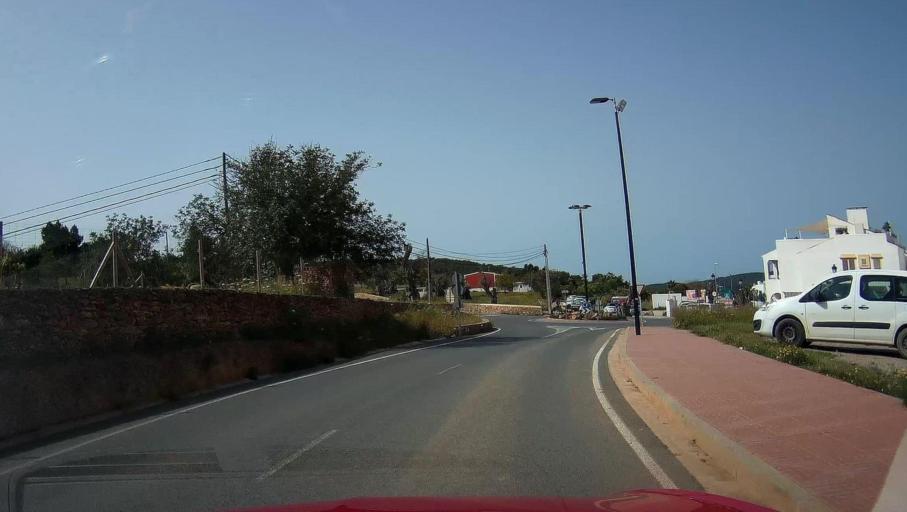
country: ES
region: Balearic Islands
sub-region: Illes Balears
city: Santa Eularia des Riu
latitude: 39.0336
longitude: 1.5660
